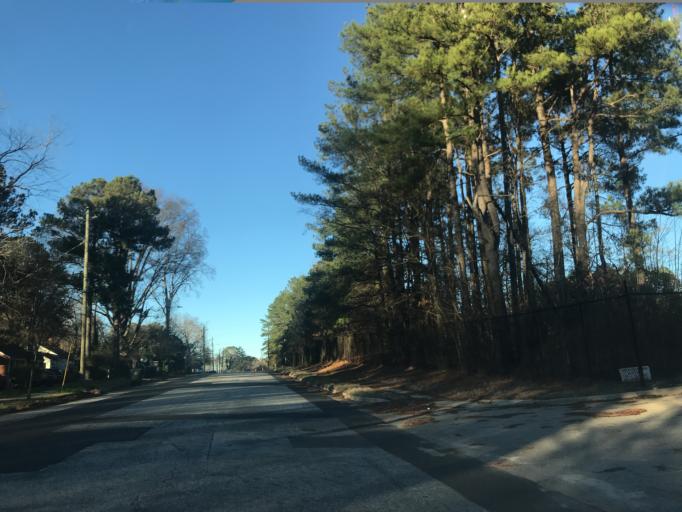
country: US
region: North Carolina
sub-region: Wake County
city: Raleigh
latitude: 35.7907
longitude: -78.6206
